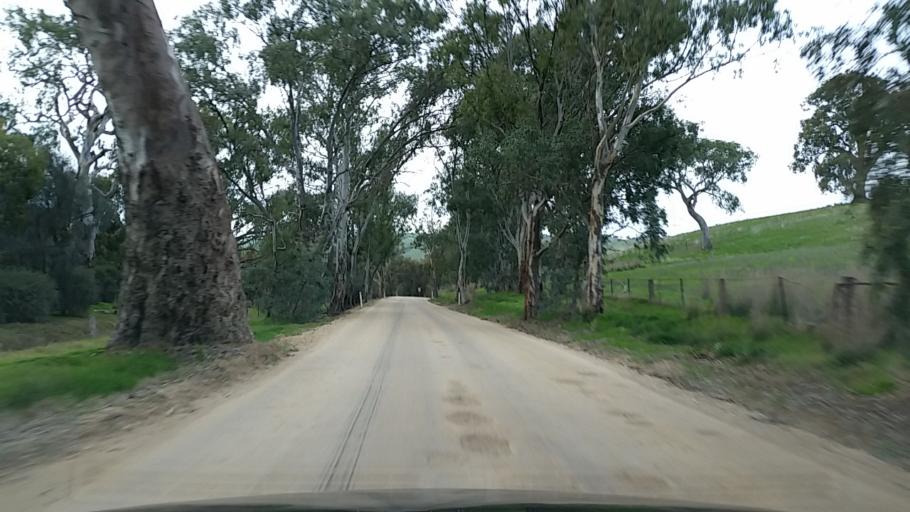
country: AU
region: South Australia
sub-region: Mount Barker
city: Nairne
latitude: -34.9551
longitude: 139.0119
